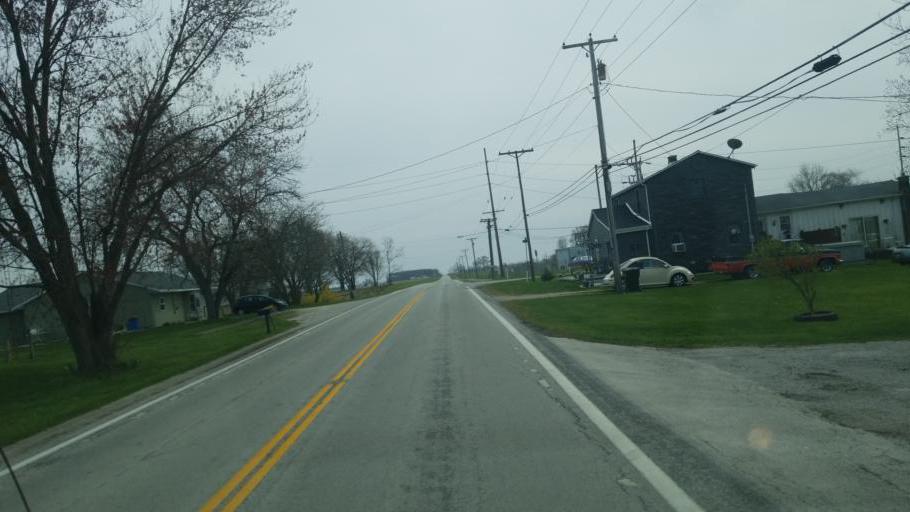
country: US
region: Ohio
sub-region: Wyandot County
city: Carey
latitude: 41.0274
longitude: -83.2969
